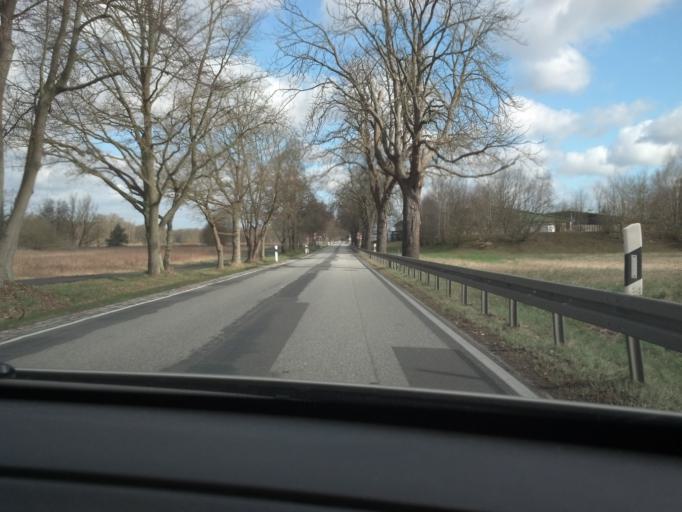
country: DE
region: Mecklenburg-Vorpommern
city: Boizenburg
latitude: 53.4134
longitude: 10.7421
